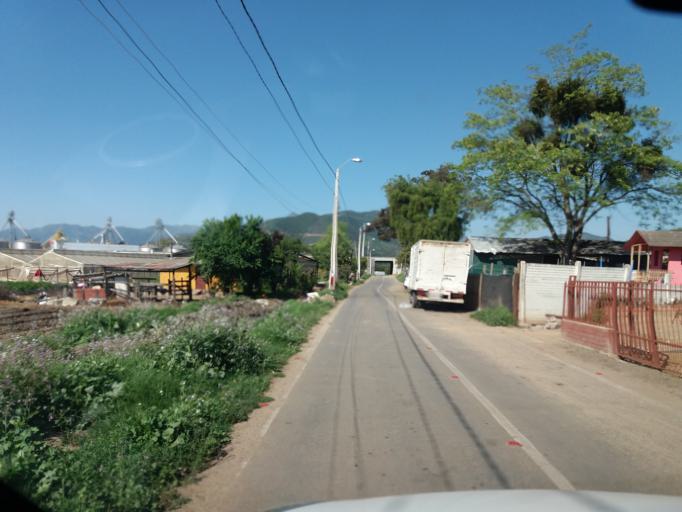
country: CL
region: Valparaiso
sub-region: Provincia de Quillota
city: Quillota
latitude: -32.9453
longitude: -71.2879
